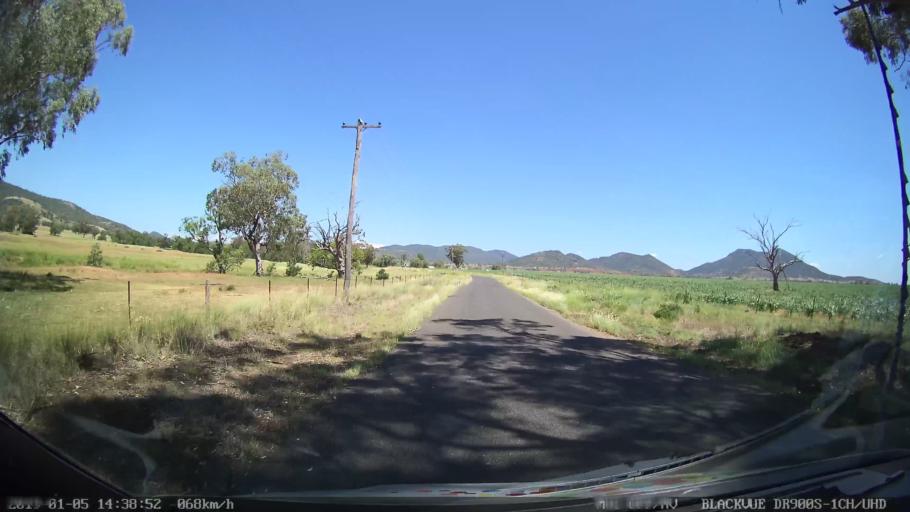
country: AU
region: New South Wales
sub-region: Tamworth Municipality
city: Phillip
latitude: -31.2519
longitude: 150.6947
